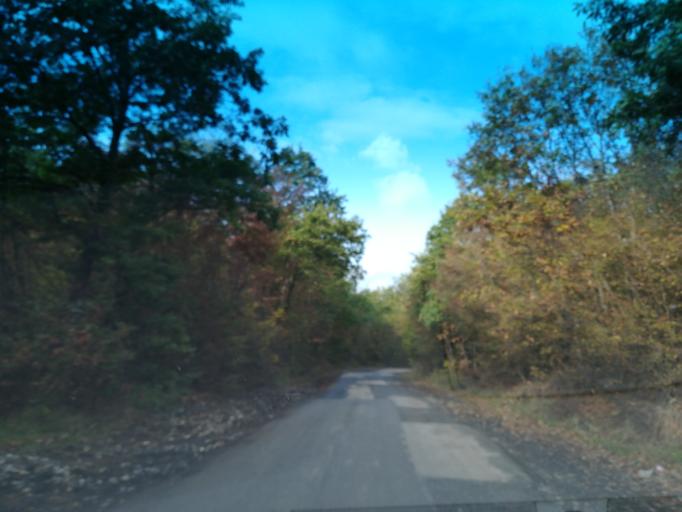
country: BG
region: Stara Zagora
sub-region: Obshtina Nikolaevo
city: Elkhovo
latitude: 42.3219
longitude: 25.4009
